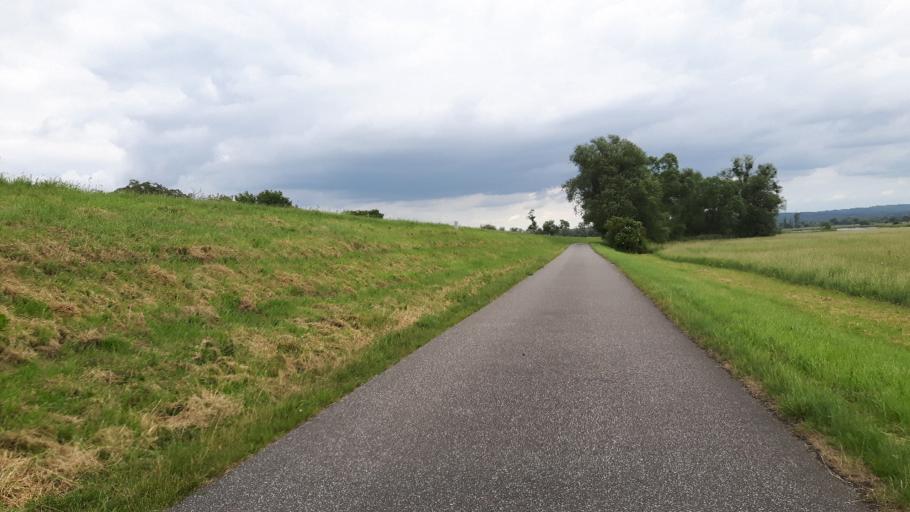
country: DE
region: Brandenburg
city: Schoneberg
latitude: 52.9867
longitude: 14.1572
